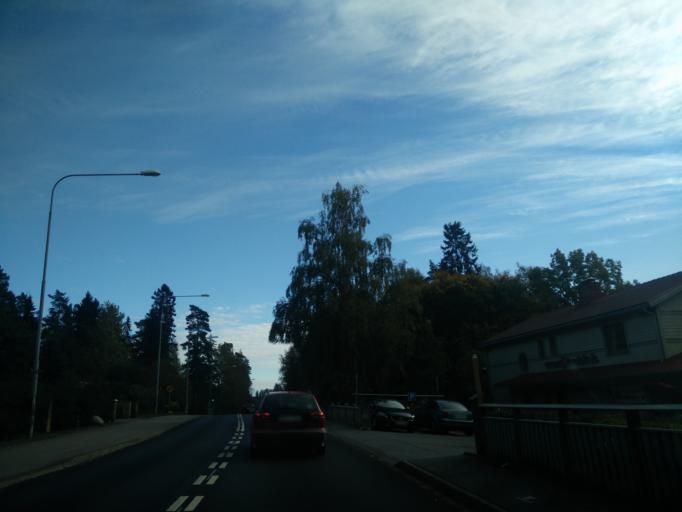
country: SE
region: Stockholm
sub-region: Upplands Vasby Kommun
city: Upplands Vaesby
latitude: 59.5123
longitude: 17.9400
